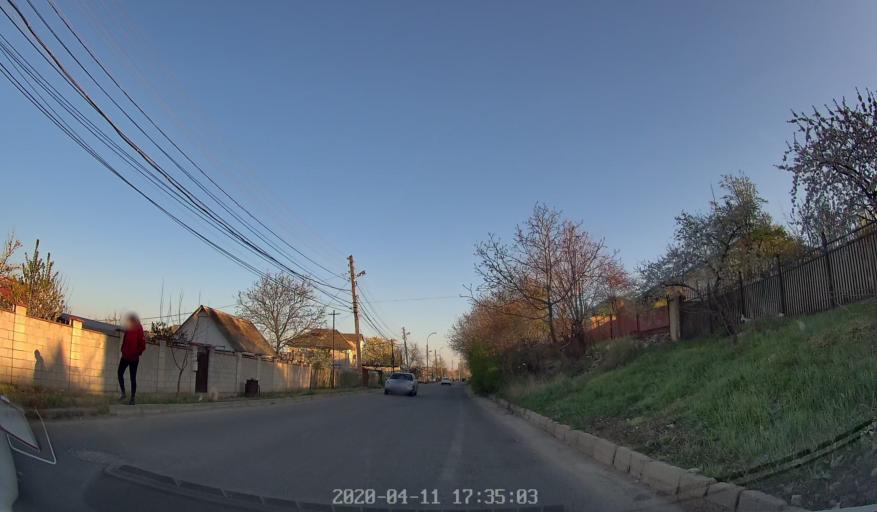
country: MD
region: Laloveni
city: Ialoveni
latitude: 46.9923
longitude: 28.8030
